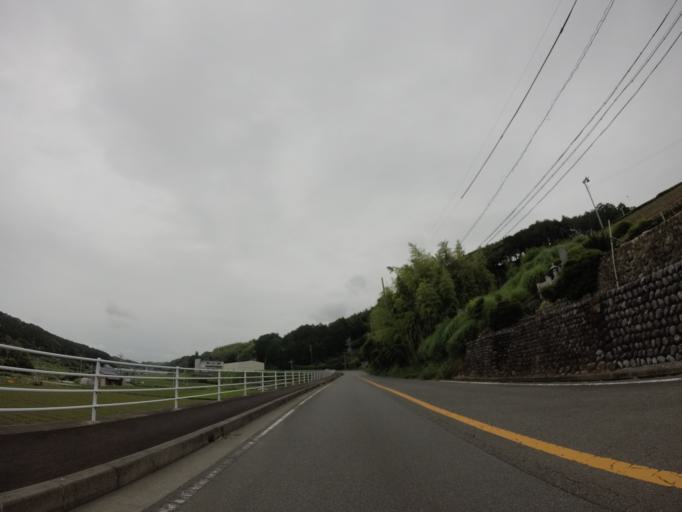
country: JP
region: Shizuoka
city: Shimada
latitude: 34.8073
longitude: 138.1737
